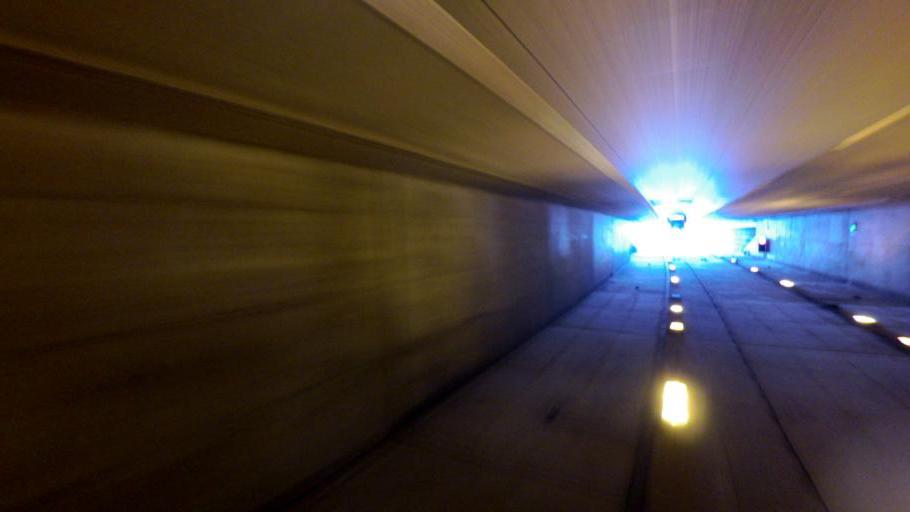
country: DE
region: Berlin
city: Altglienicke
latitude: 52.4056
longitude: 13.5213
